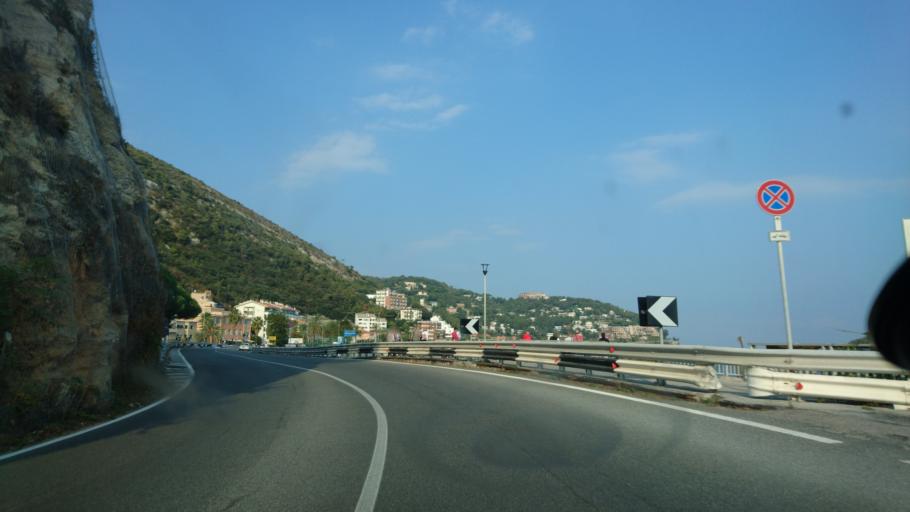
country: IT
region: Liguria
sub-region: Provincia di Savona
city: Spotorno
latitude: 44.2326
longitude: 8.4276
